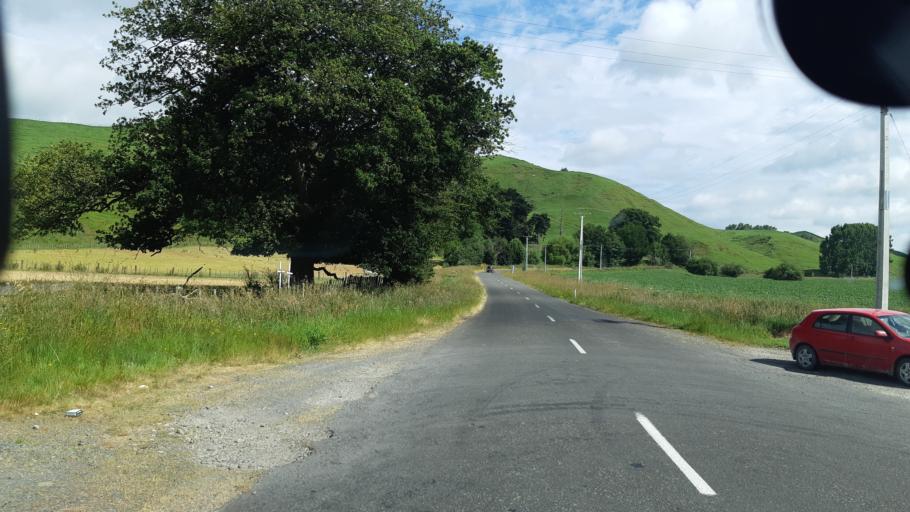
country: NZ
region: Manawatu-Wanganui
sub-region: Rangitikei District
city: Bulls
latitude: -39.9650
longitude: 175.5242
